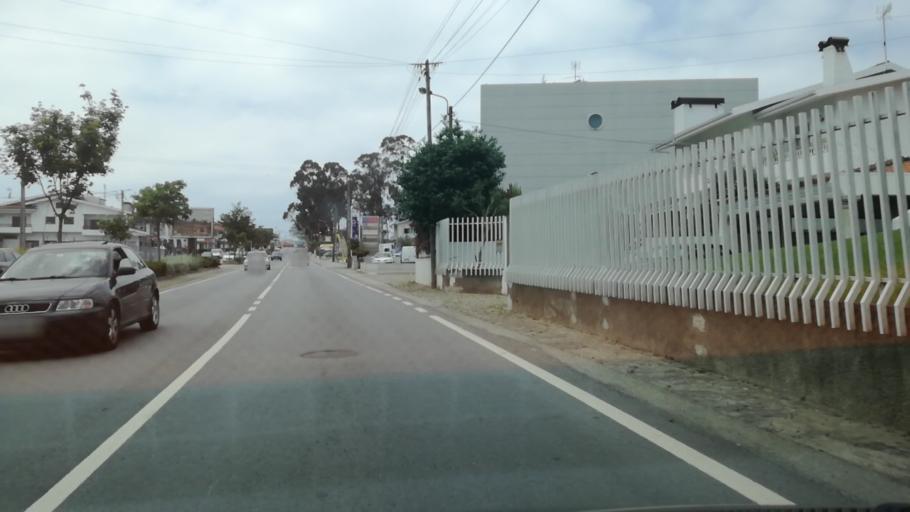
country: PT
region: Porto
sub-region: Trofa
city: Sao Romao do Coronado
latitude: 41.3064
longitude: -8.5849
